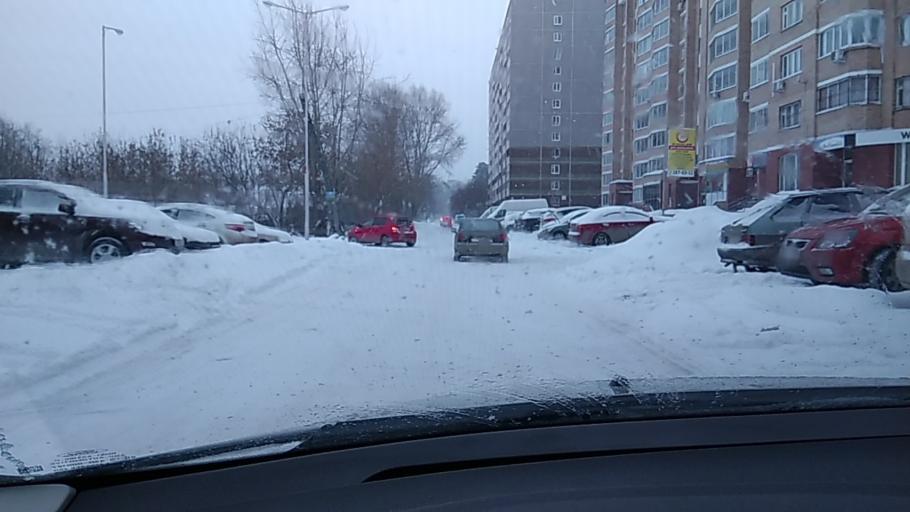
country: RU
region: Sverdlovsk
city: Sovkhoznyy
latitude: 56.8204
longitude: 60.5454
